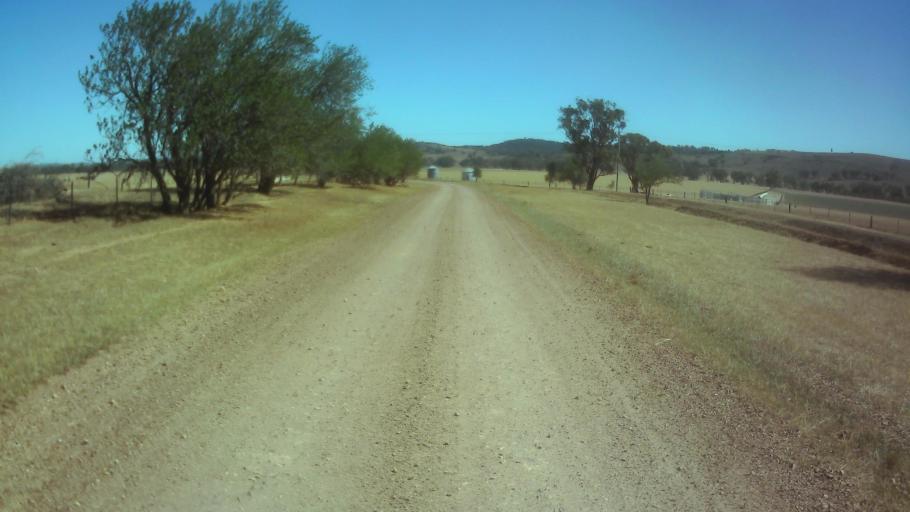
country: AU
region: New South Wales
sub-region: Weddin
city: Grenfell
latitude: -33.9554
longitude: 148.3023
